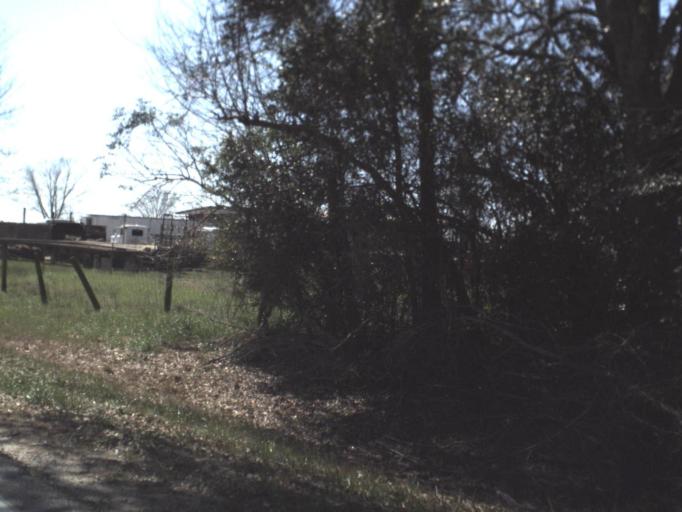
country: US
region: Florida
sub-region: Gadsden County
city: Gretna
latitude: 30.7025
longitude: -84.6254
